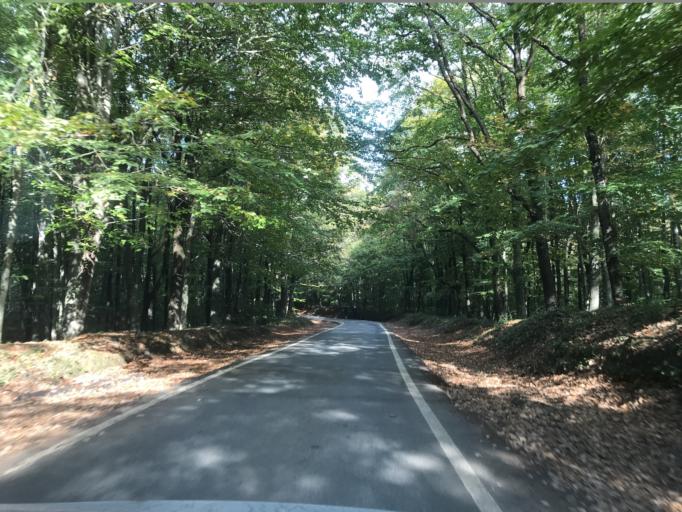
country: TR
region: Istanbul
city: Arikoey
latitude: 41.1851
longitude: 28.9855
